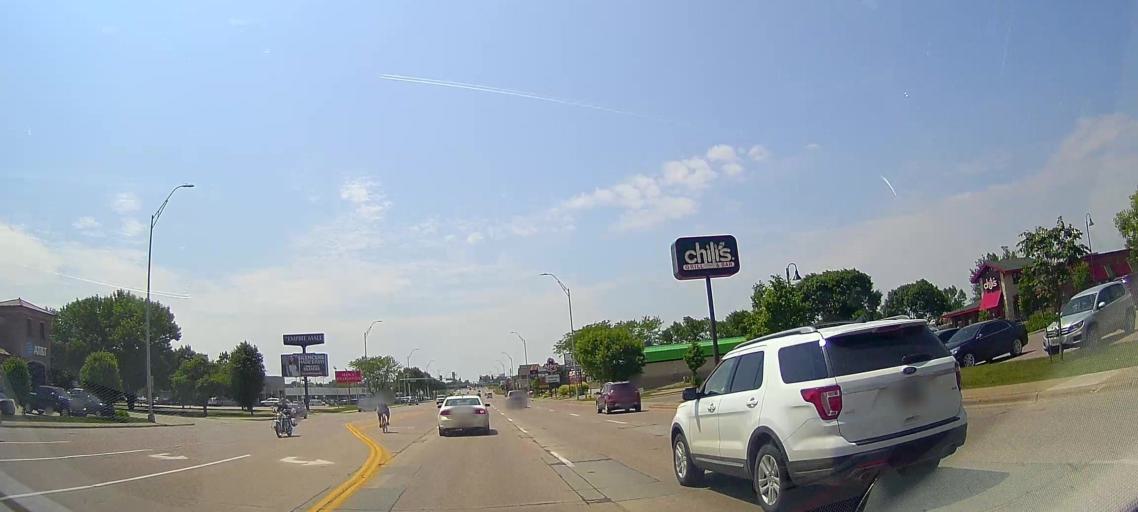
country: US
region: South Dakota
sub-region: Minnehaha County
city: Sioux Falls
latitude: 43.5150
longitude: -96.7724
